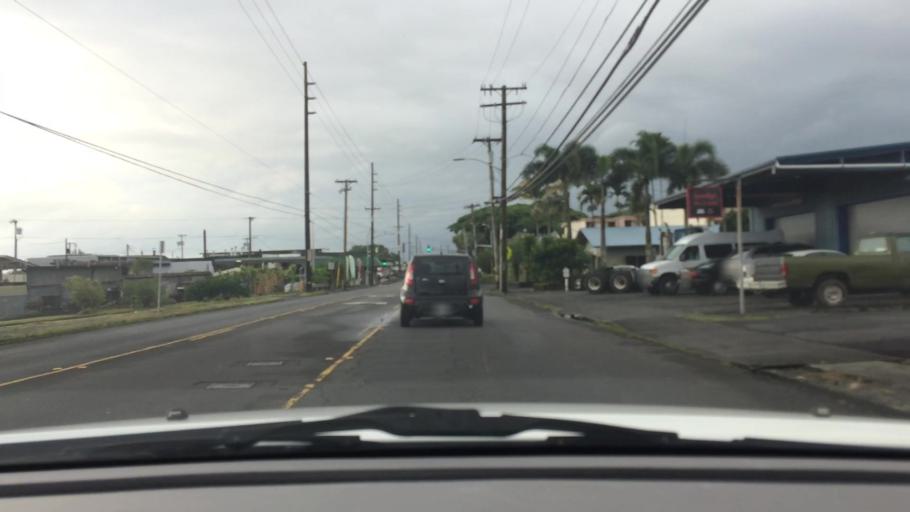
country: US
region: Hawaii
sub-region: Hawaii County
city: Hilo
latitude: 19.7173
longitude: -155.0841
